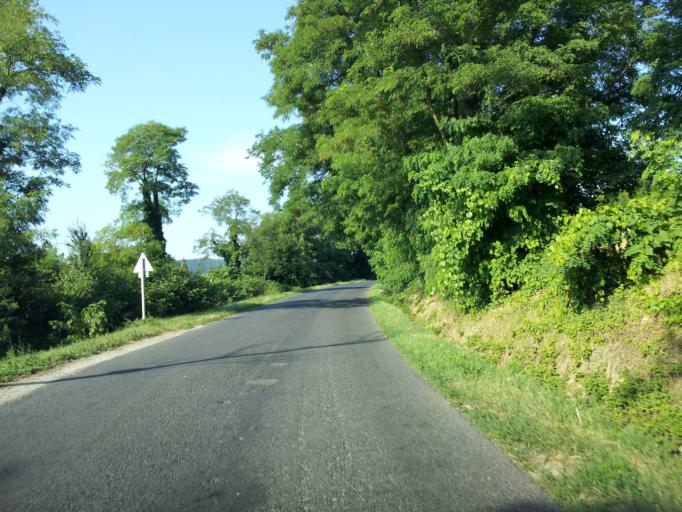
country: HU
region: Veszprem
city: Tapolca
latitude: 46.8493
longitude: 17.3546
